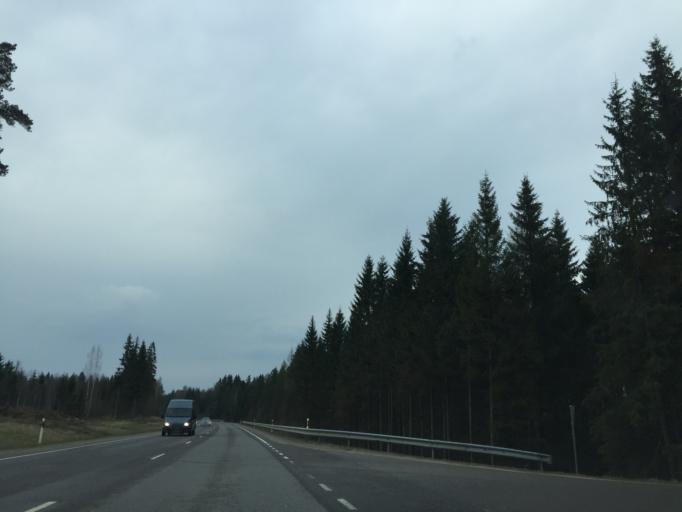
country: EE
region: Tartu
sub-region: UElenurme vald
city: Ulenurme
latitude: 58.0985
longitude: 26.7400
